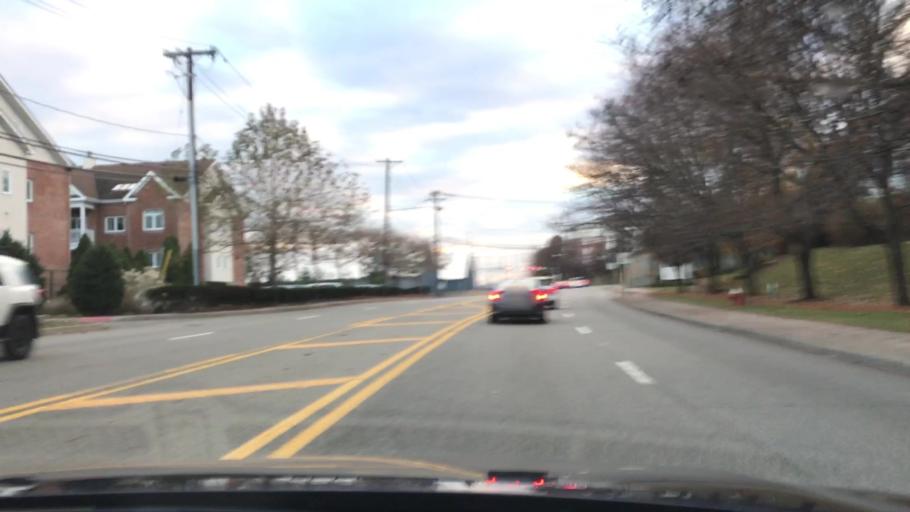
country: US
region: New Jersey
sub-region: Bergen County
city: Edgewater
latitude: 40.8224
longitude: -73.9761
